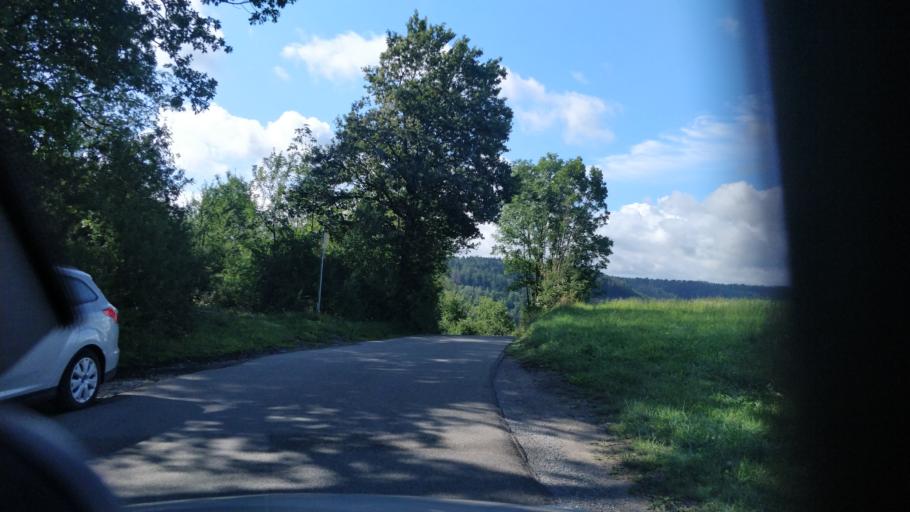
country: DE
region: Baden-Wuerttemberg
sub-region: Regierungsbezirk Stuttgart
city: Oberrot
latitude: 48.9874
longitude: 9.6795
